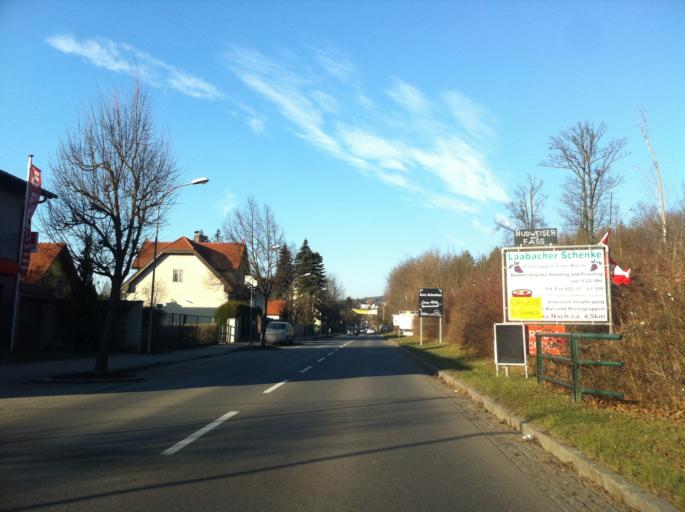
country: AT
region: Lower Austria
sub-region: Politischer Bezirk Wien-Umgebung
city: Gablitz
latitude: 48.2213
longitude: 16.1632
